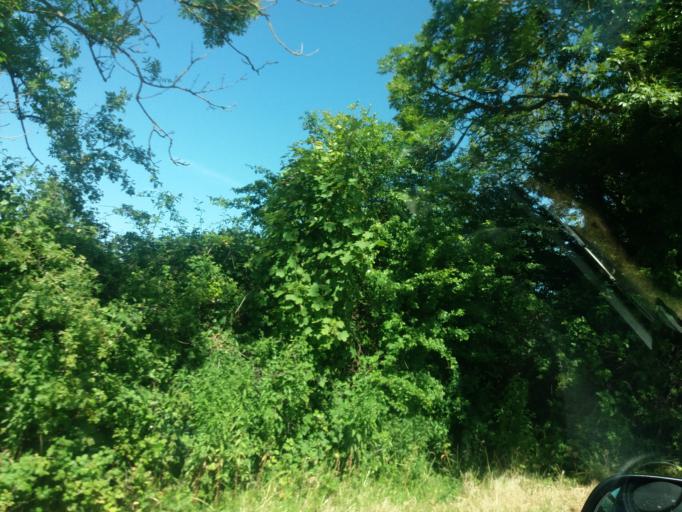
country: IE
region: Leinster
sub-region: Dublin City
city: Finglas
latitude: 53.4385
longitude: -6.3105
